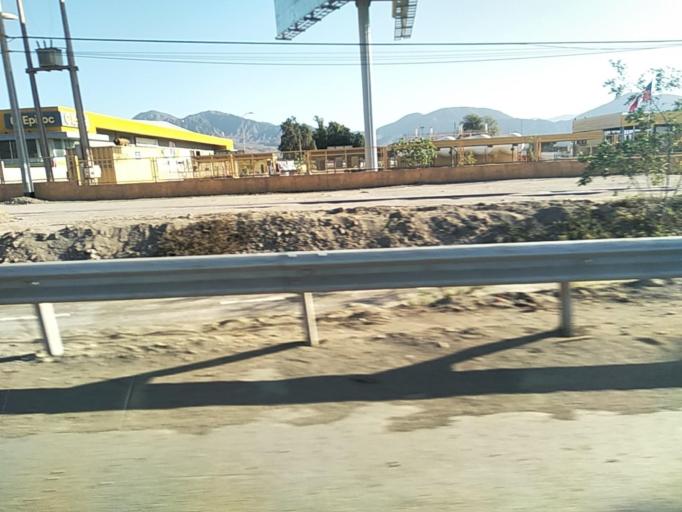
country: CL
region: Atacama
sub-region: Provincia de Copiapo
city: Copiapo
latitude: -27.3349
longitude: -70.3776
